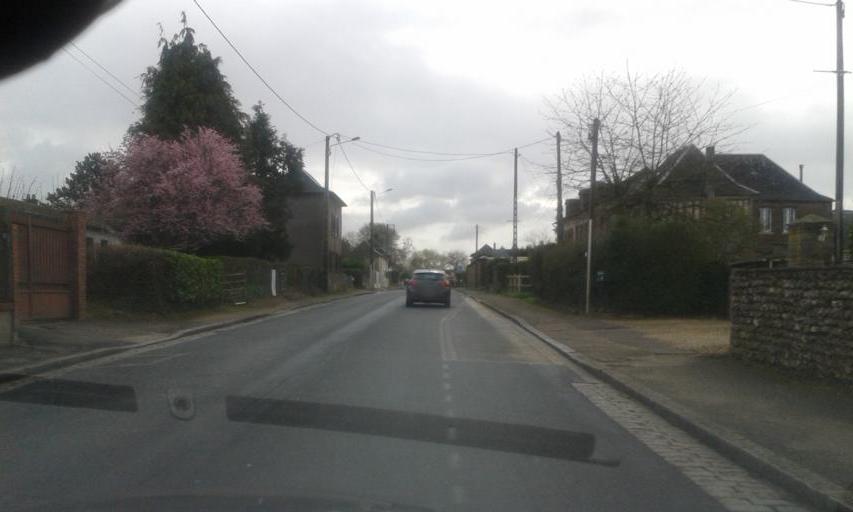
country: FR
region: Haute-Normandie
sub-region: Departement de l'Eure
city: Fleury-sur-Andelle
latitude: 49.3859
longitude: 1.3093
